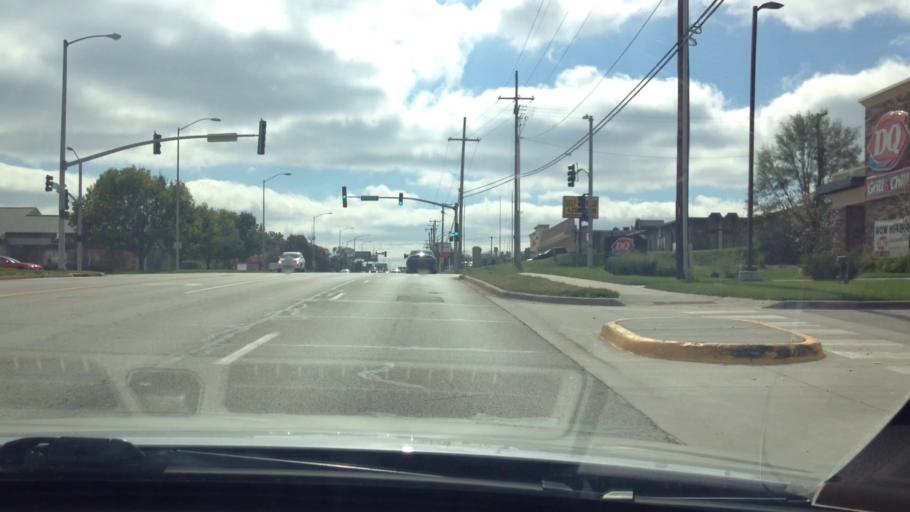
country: US
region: Missouri
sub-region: Clay County
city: Gladstone
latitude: 39.2491
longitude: -94.5760
